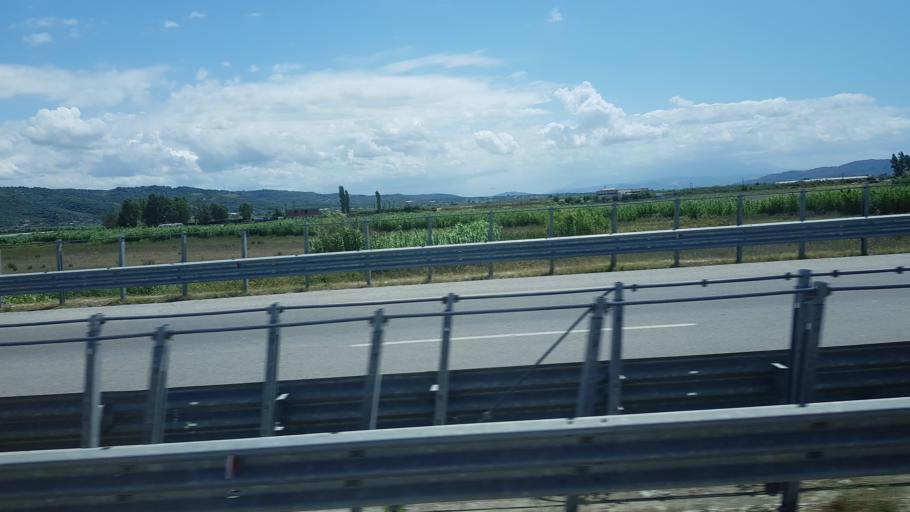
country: AL
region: Fier
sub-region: Rrethi i Fierit
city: Levan
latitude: 40.6632
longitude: 19.4747
